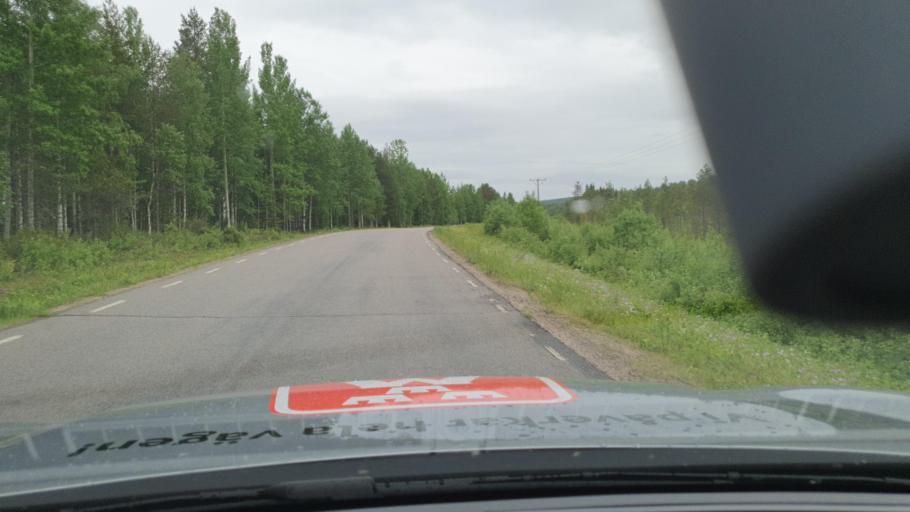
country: SE
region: Norrbotten
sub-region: Pajala Kommun
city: Pajala
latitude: 66.7445
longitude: 23.1712
